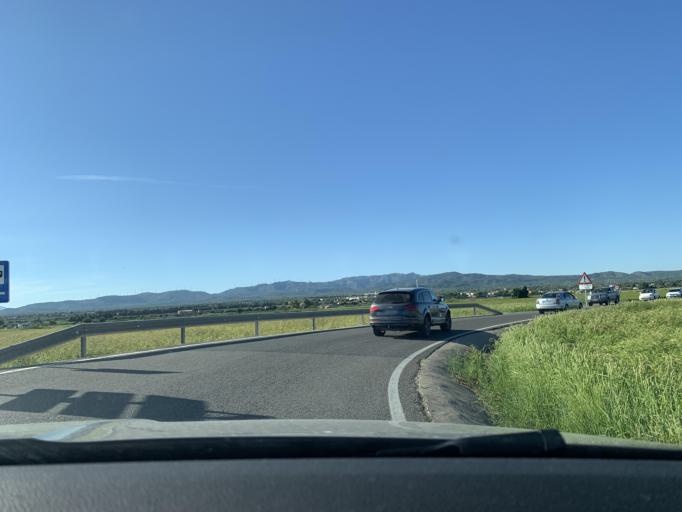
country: ES
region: Catalonia
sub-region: Provincia de Tarragona
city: Camarles
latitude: 40.7763
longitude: 0.6892
